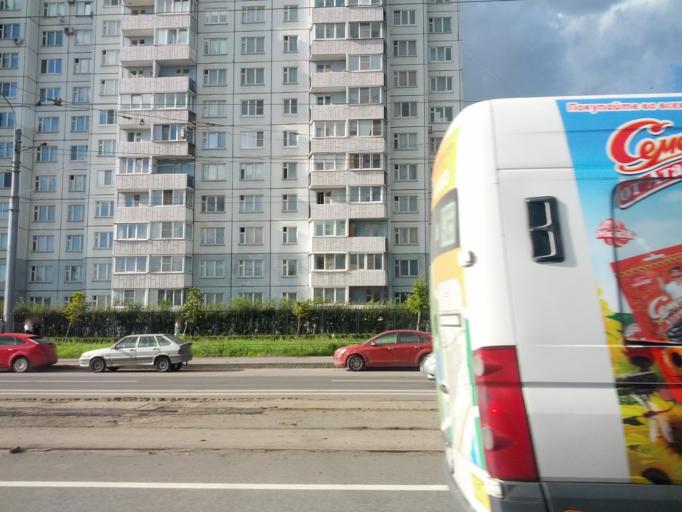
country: RU
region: St.-Petersburg
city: Krasnogvargeisky
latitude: 59.9088
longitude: 30.4932
